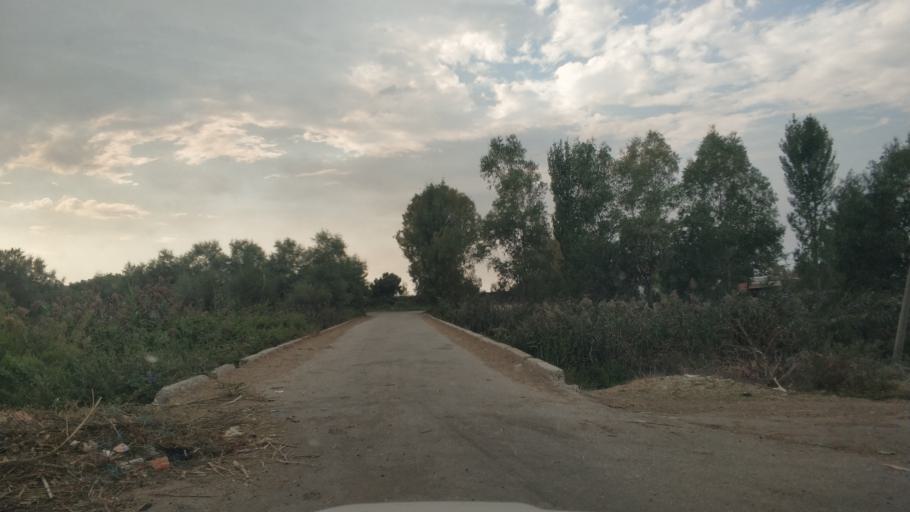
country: AL
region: Fier
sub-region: Rrethi i Fierit
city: Dermenas
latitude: 40.7310
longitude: 19.4664
